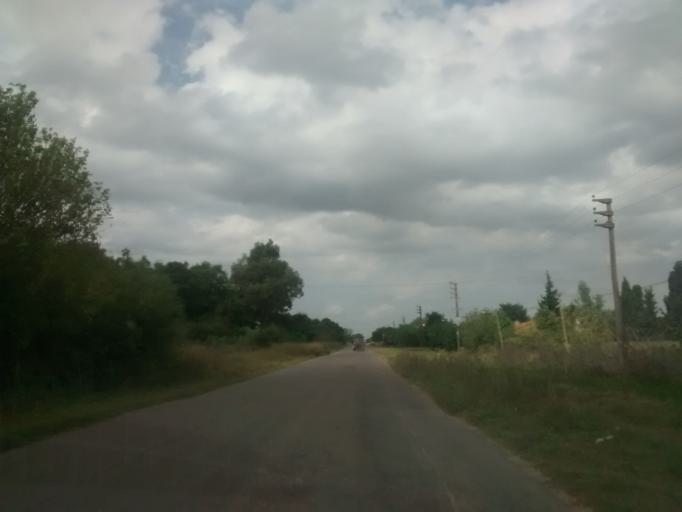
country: AR
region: Buenos Aires
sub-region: Partido de La Plata
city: La Plata
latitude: -34.9882
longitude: -57.9204
